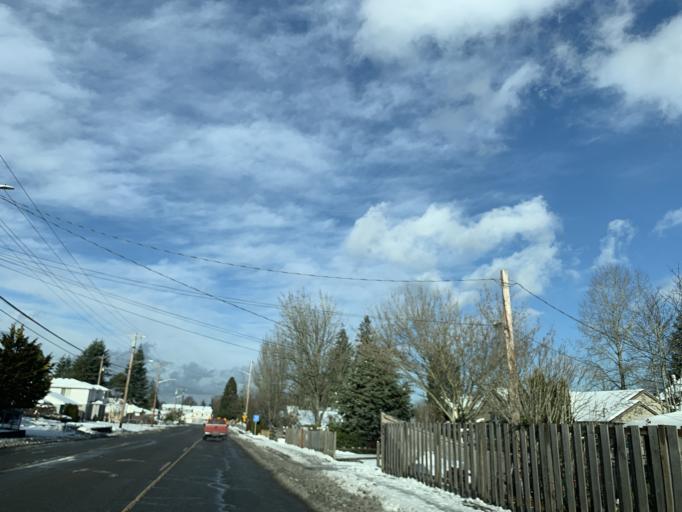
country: US
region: Washington
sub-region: Snohomish County
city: Martha Lake
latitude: 47.9152
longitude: -122.2391
